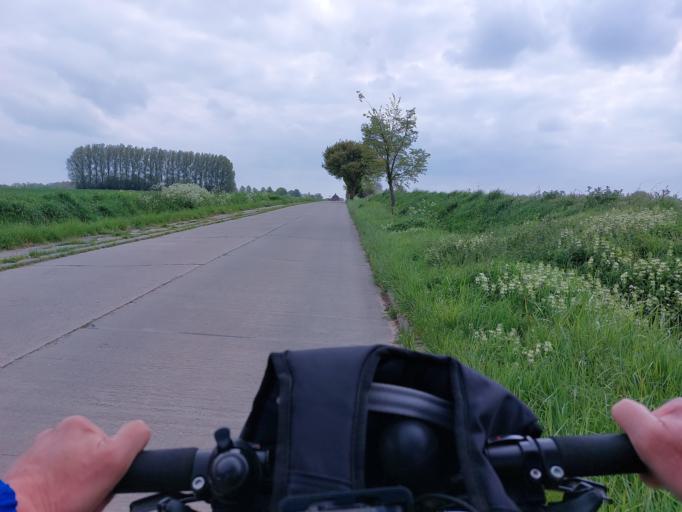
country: BE
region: Wallonia
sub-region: Province du Hainaut
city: Dour
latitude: 50.3557
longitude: 3.7401
